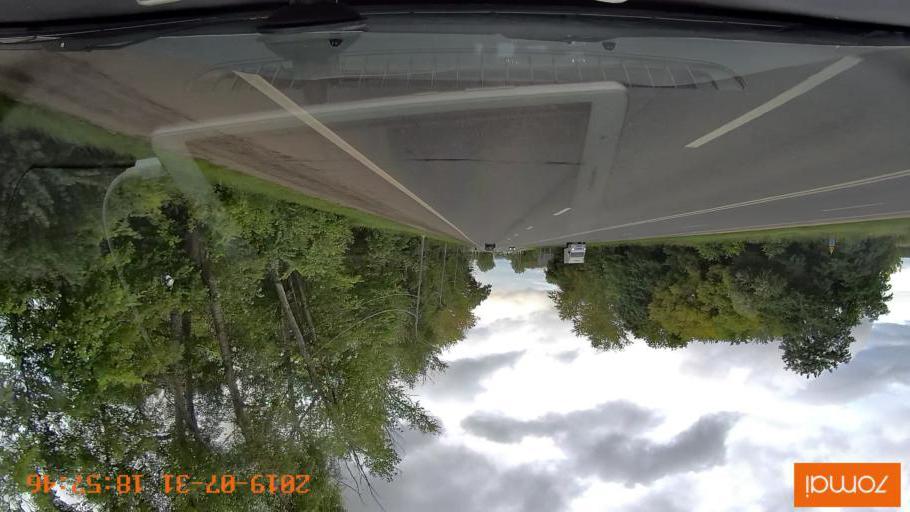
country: RU
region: Moskovskaya
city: Raduzhnyy
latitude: 55.1516
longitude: 38.6962
